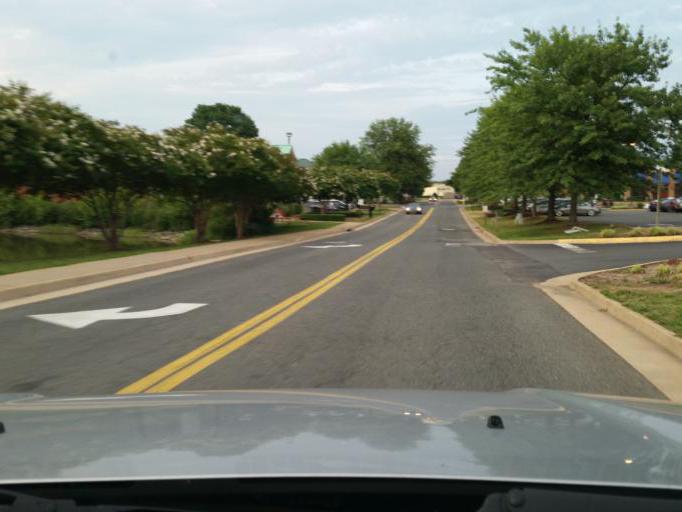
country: US
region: Virginia
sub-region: Stafford County
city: Falmouth
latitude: 38.2970
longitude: -77.5123
